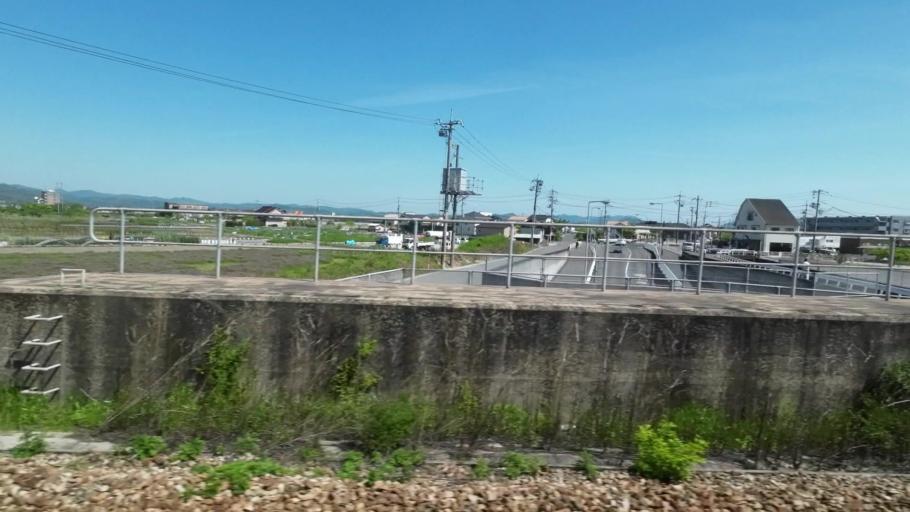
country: JP
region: Hiroshima
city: Onomichi
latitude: 34.4391
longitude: 133.2364
